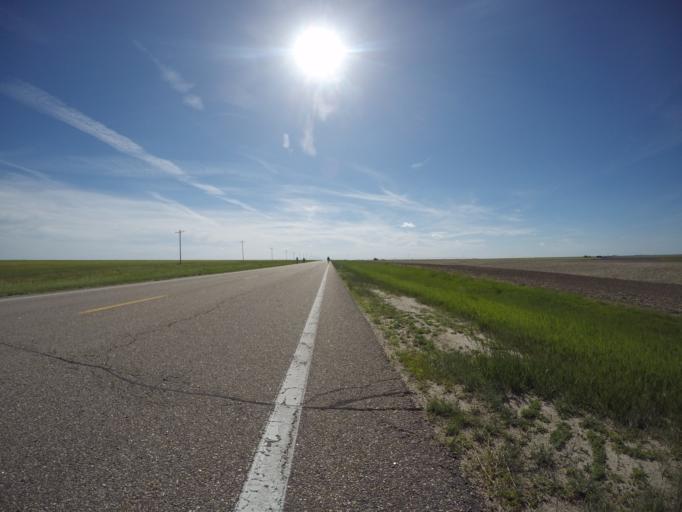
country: US
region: Kansas
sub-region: Cheyenne County
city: Saint Francis
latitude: 39.7566
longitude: -101.9979
